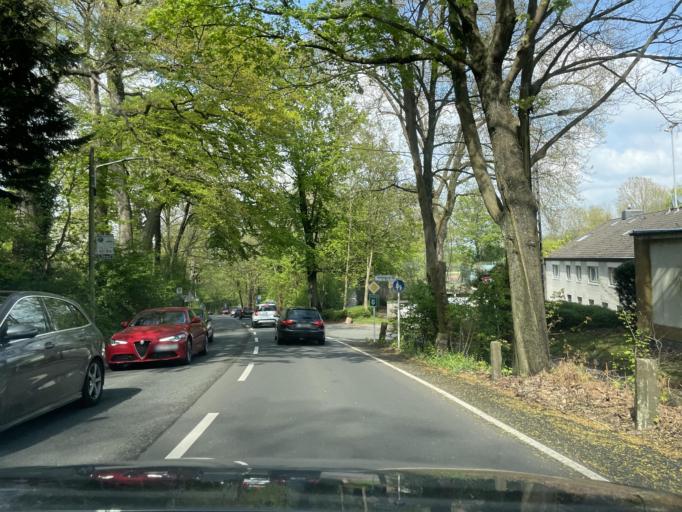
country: DE
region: North Rhine-Westphalia
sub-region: Regierungsbezirk Dusseldorf
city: Wuppertal
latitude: 51.2520
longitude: 7.1786
